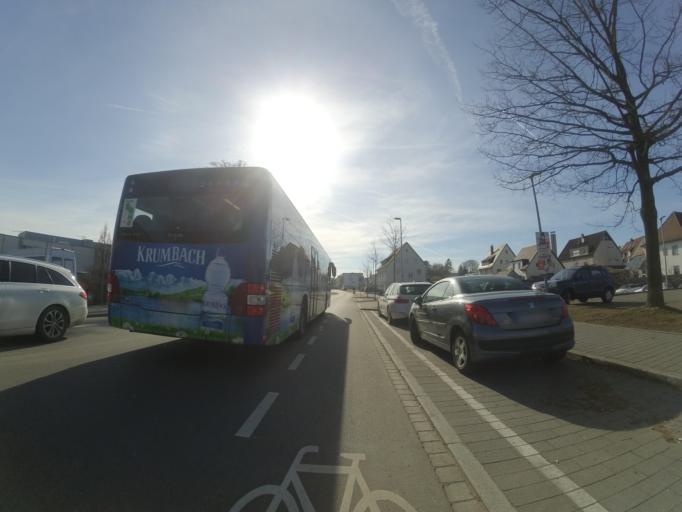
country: DE
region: Baden-Wuerttemberg
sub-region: Tuebingen Region
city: Friedrichshafen
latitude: 47.6588
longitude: 9.4866
